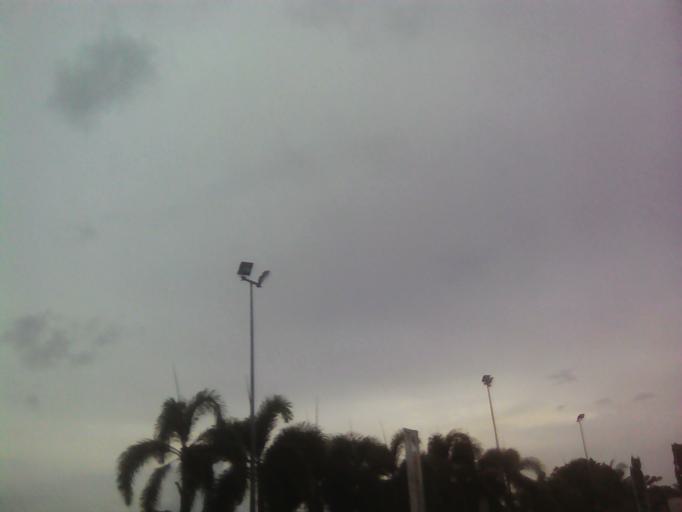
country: MY
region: Penang
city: Perai
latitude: 5.4052
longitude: 100.3920
